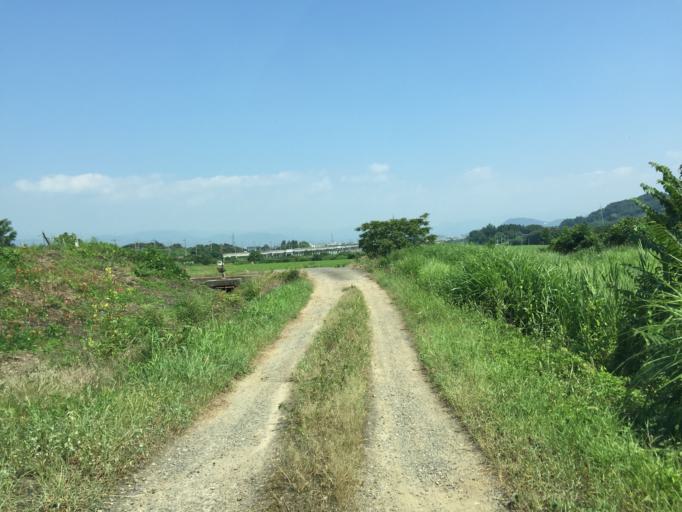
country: JP
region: Fukushima
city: Fukushima-shi
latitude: 37.7041
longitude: 140.4555
